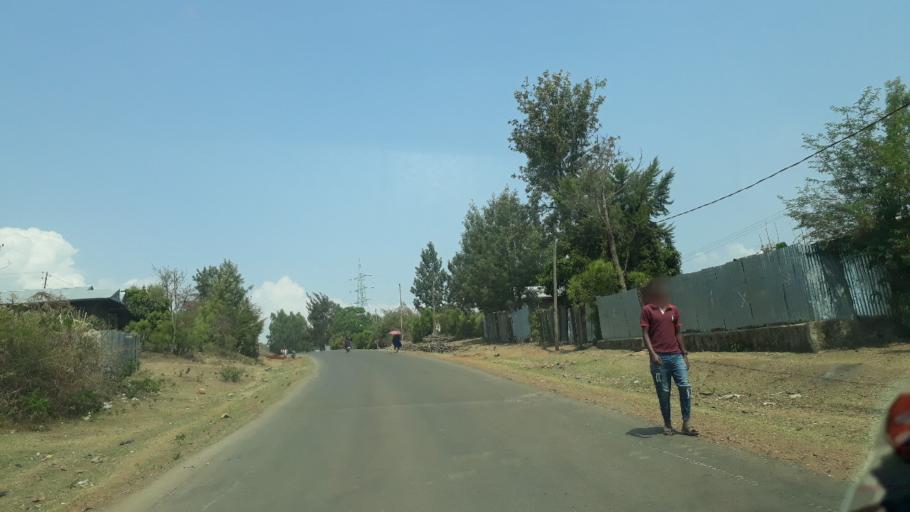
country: ET
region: Oromiya
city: Agaro
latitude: 8.0004
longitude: 36.4974
